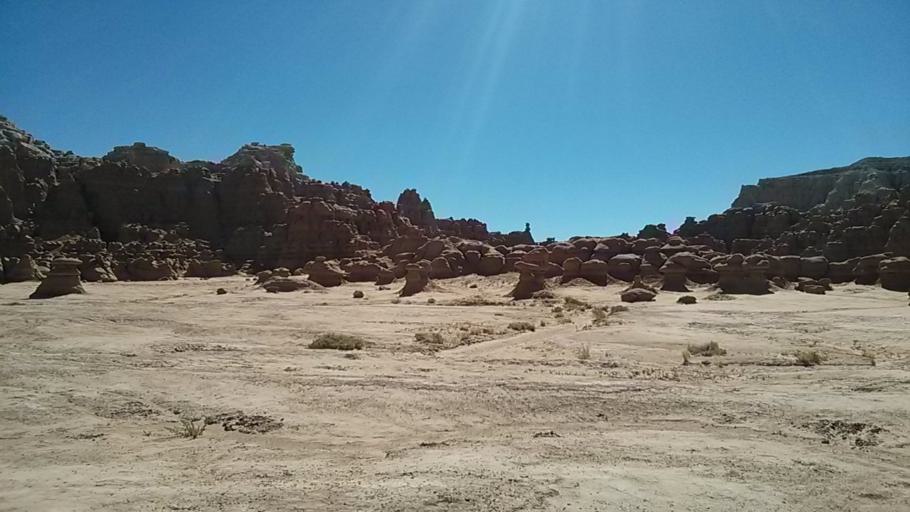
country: US
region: Utah
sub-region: Emery County
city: Ferron
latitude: 38.5641
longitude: -110.6993
